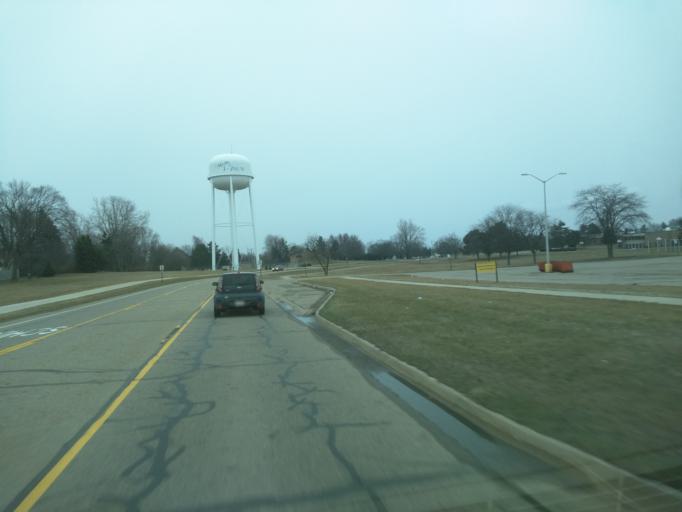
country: US
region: Michigan
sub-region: Eaton County
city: Waverly
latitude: 42.7306
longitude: -84.6205
